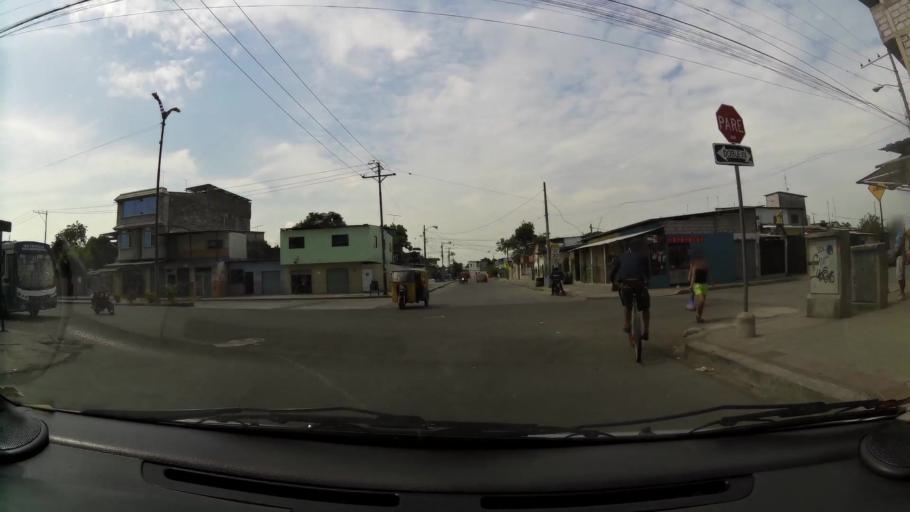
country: EC
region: Guayas
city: Guayaquil
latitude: -2.2833
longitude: -79.8842
